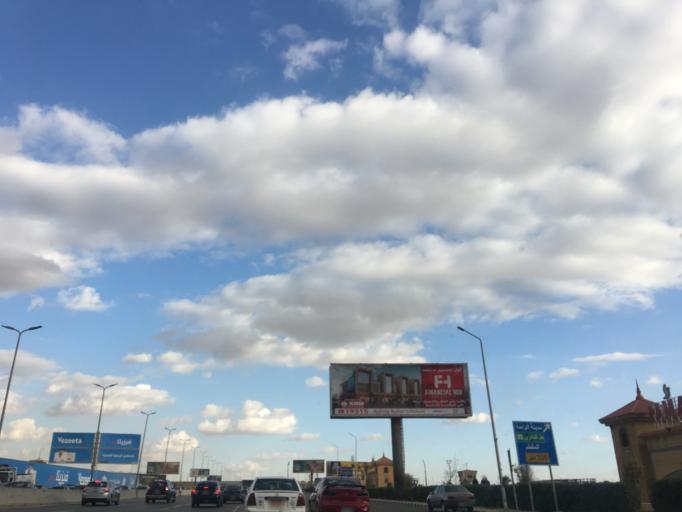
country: EG
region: Muhafazat al Qahirah
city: Cairo
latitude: 30.0241
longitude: 31.3637
